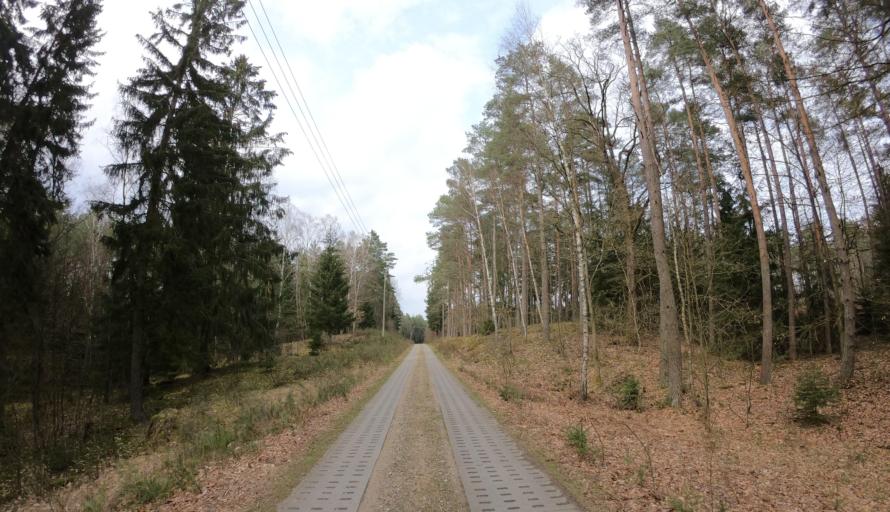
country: PL
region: West Pomeranian Voivodeship
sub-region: Powiat swidwinski
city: Rabino
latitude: 53.8656
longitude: 15.8716
